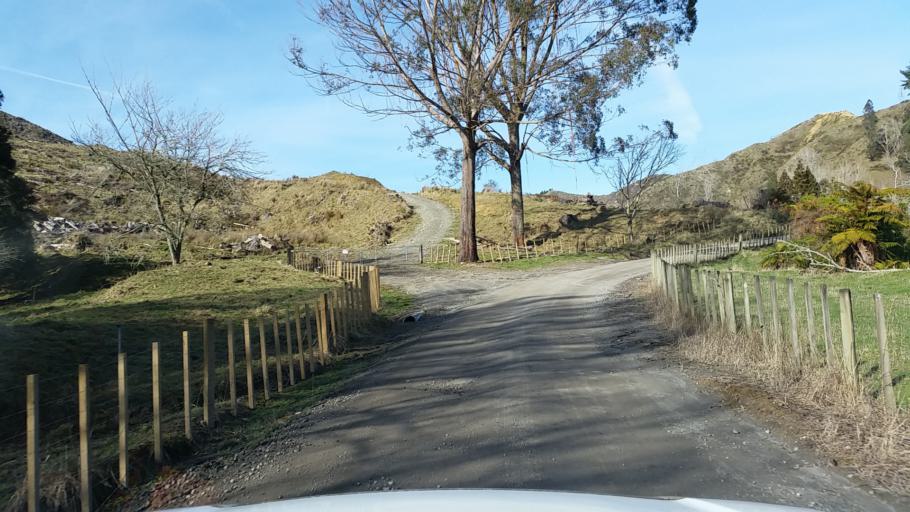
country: NZ
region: Taranaki
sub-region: South Taranaki District
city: Eltham
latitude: -39.3567
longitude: 174.5119
